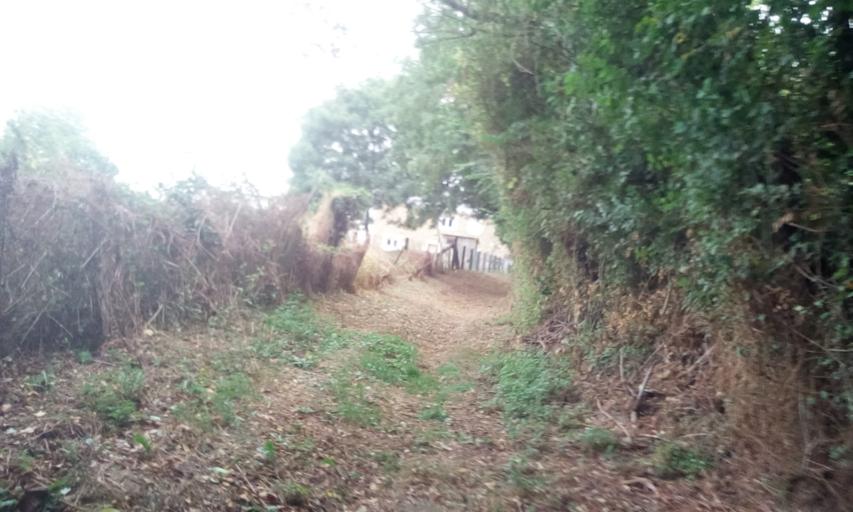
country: FR
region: Lower Normandy
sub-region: Departement du Calvados
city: Thury-Harcourt
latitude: 48.9911
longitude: -0.4285
